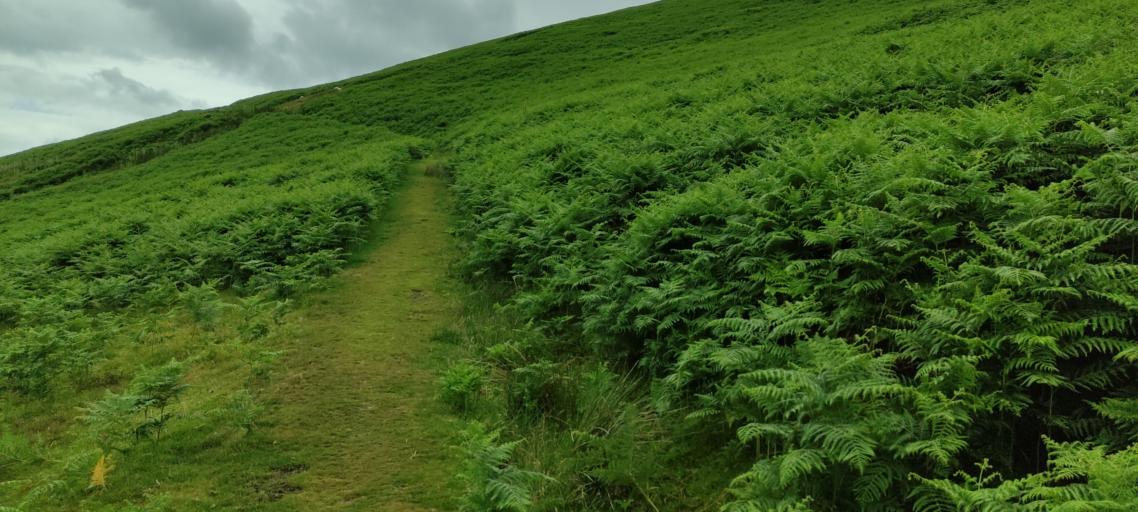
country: GB
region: England
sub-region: Cumbria
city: Keswick
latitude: 54.6564
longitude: -2.9909
